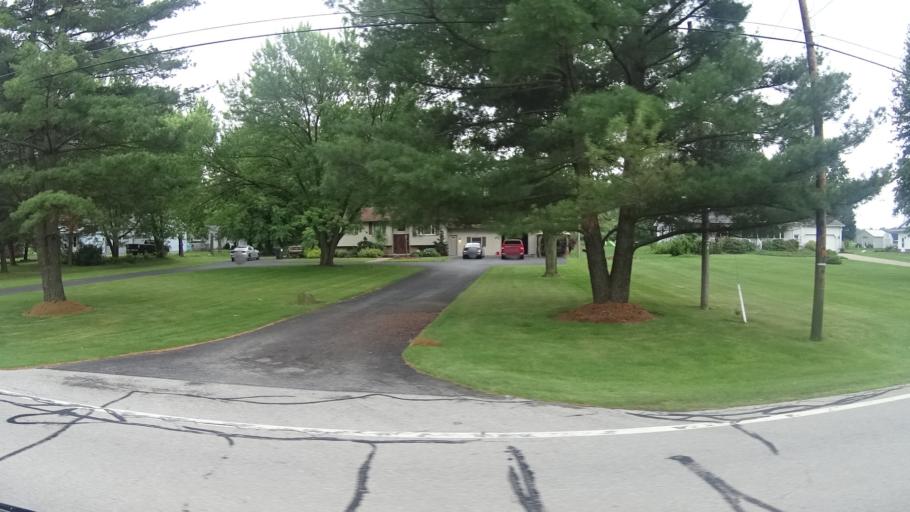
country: US
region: Ohio
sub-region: Erie County
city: Milan
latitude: 41.3013
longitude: -82.5394
